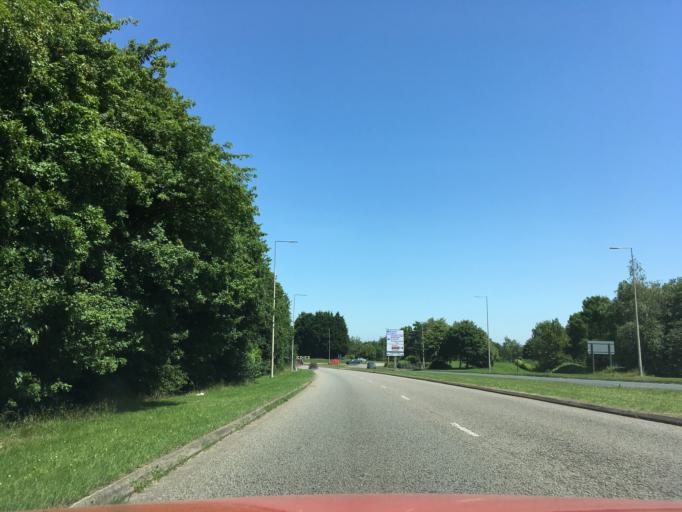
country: GB
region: England
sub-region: Milton Keynes
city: Shenley Church End
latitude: 52.0213
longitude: -0.7789
